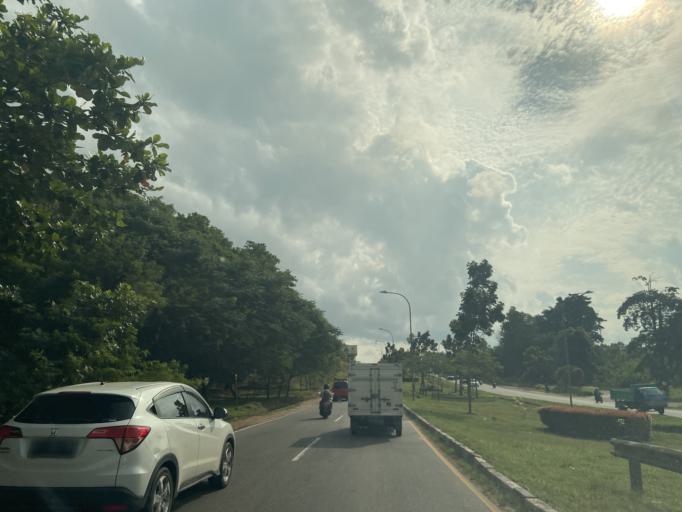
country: SG
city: Singapore
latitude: 1.0994
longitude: 104.0703
